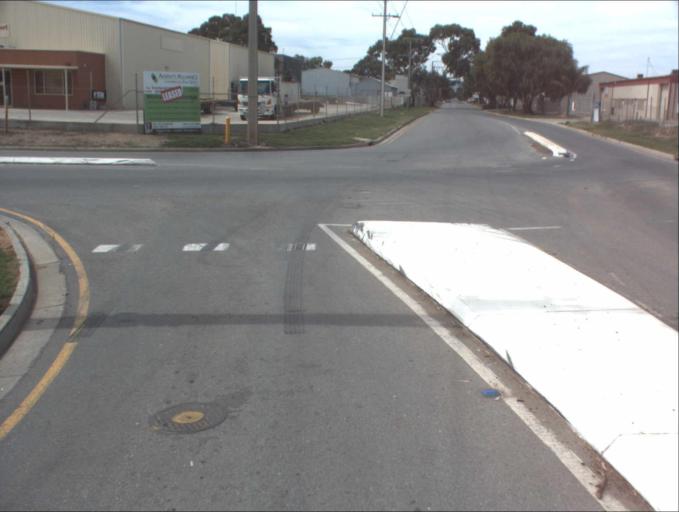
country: AU
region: South Australia
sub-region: Charles Sturt
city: Woodville North
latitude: -34.8394
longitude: 138.5502
